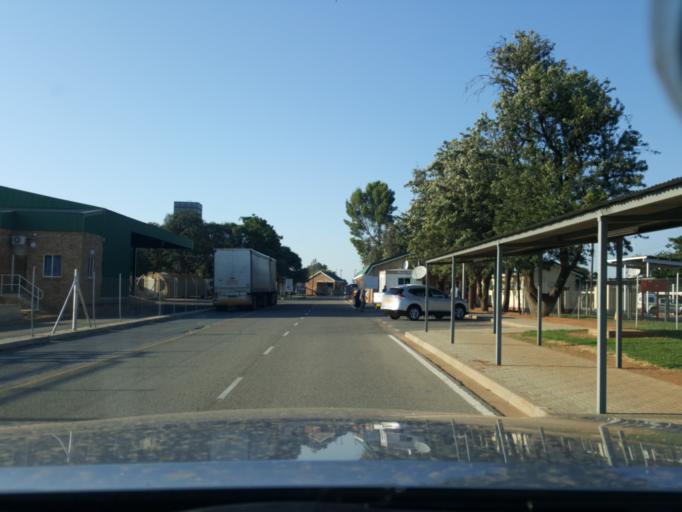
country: ZA
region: North-West
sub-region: Ngaka Modiri Molema District Municipality
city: Mmabatho
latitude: -25.6480
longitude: 25.5757
